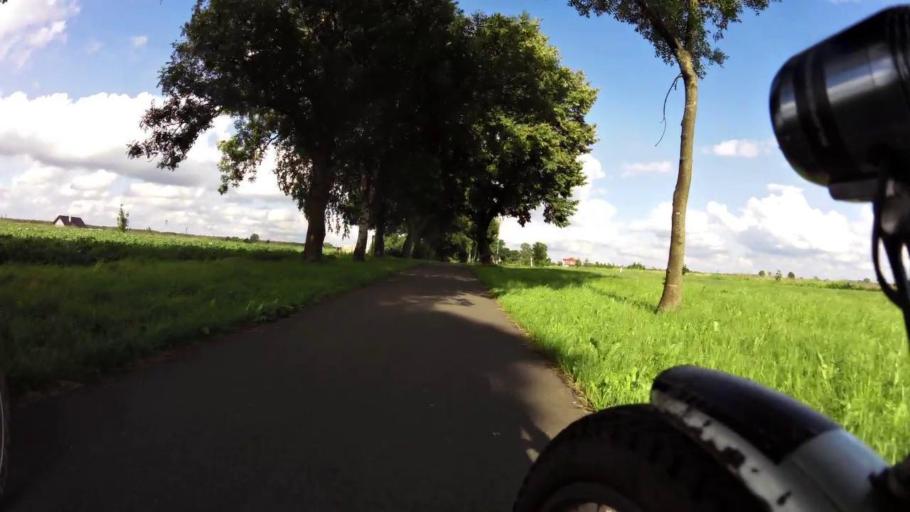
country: PL
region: West Pomeranian Voivodeship
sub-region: Powiat swidwinski
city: Swidwin
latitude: 53.7764
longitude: 15.8117
